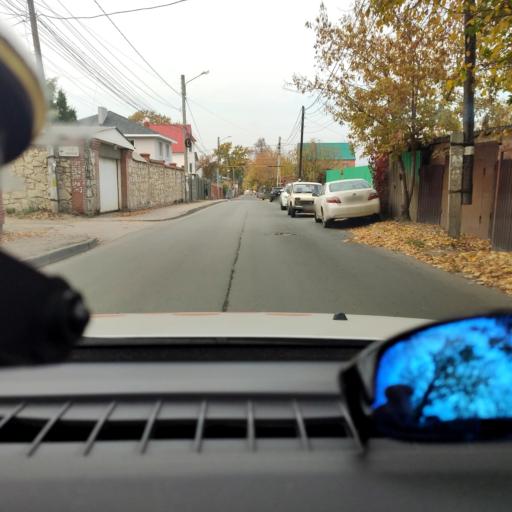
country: RU
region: Samara
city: Samara
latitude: 53.2558
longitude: 50.1897
